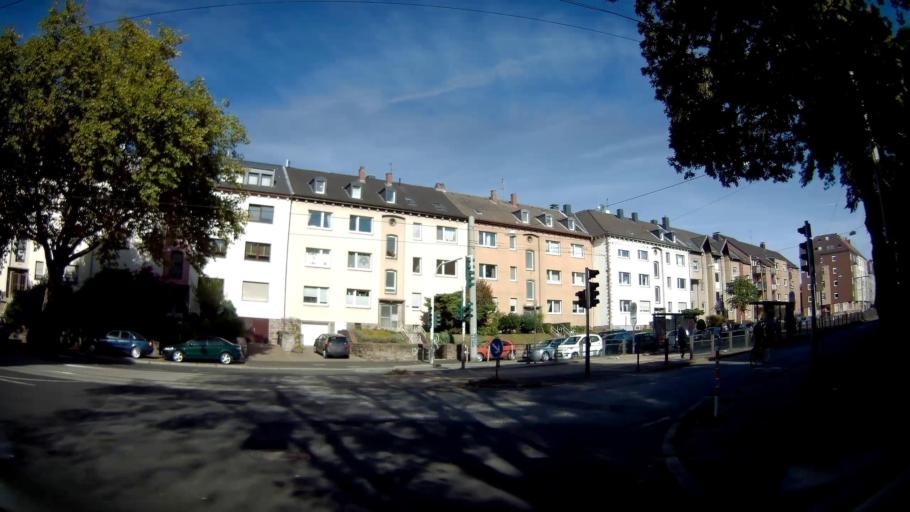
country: DE
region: North Rhine-Westphalia
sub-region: Regierungsbezirk Arnsberg
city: Bochum
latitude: 51.4685
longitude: 7.2087
